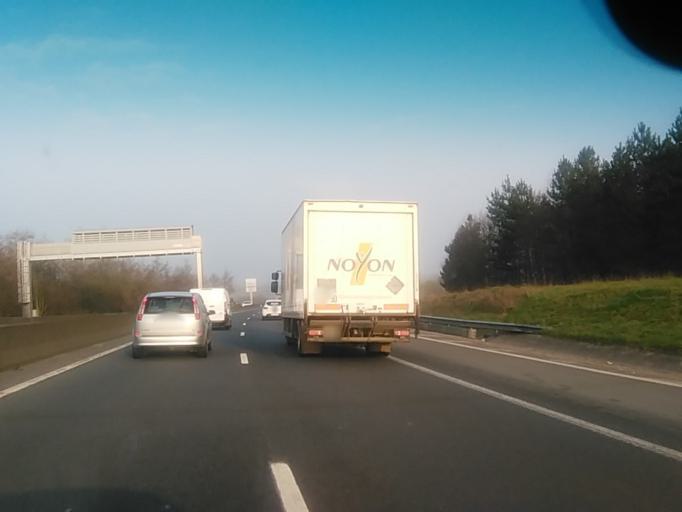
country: FR
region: Lower Normandy
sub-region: Departement du Calvados
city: Louvigny
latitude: 49.1376
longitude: -0.3924
